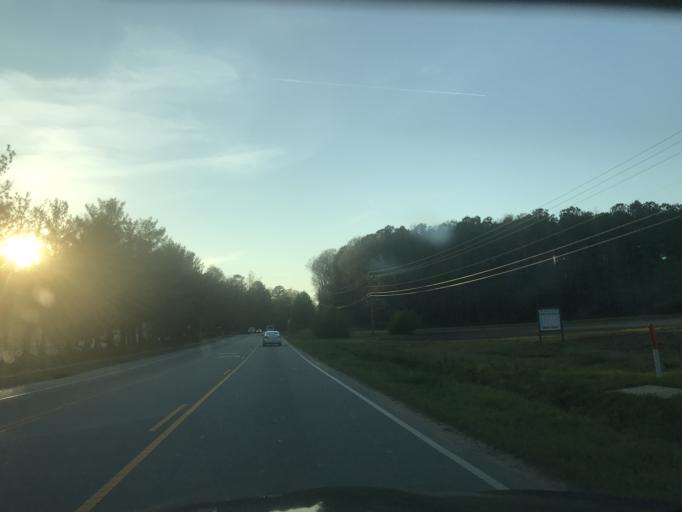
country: US
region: North Carolina
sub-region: Wake County
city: Knightdale
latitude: 35.7579
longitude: -78.5468
